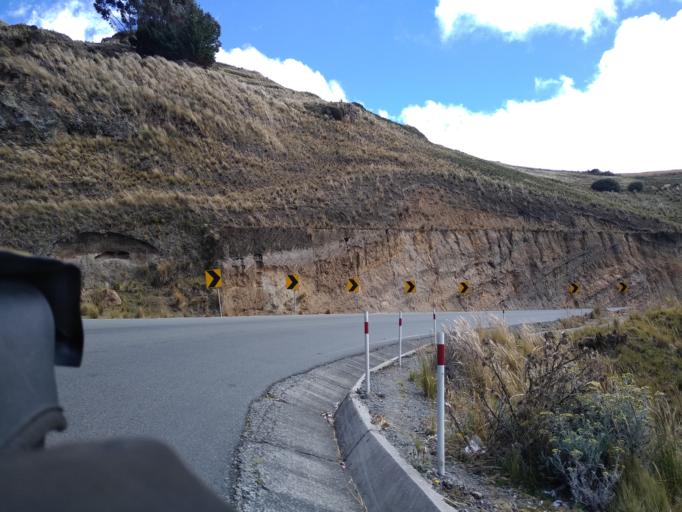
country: EC
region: Cotopaxi
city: Pujili
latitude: -0.9567
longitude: -78.9124
